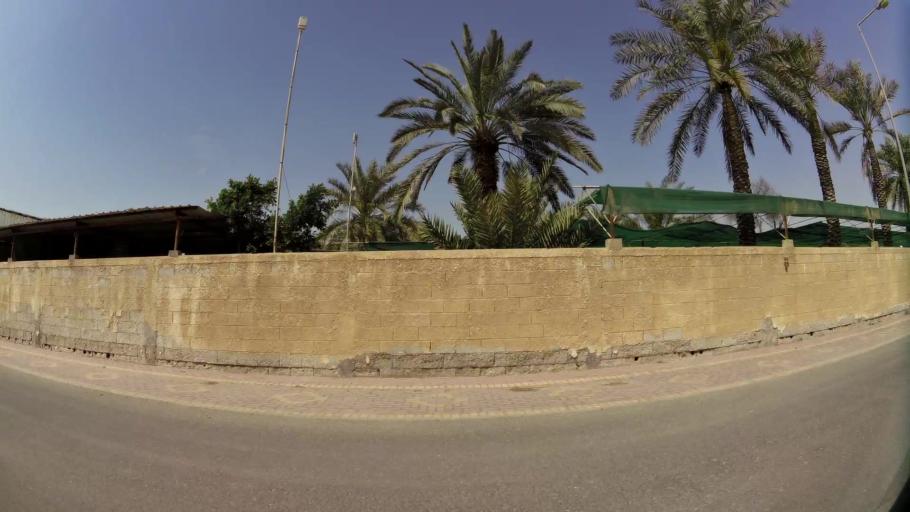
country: BH
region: Central Governorate
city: Madinat Hamad
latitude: 26.1908
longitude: 50.4591
